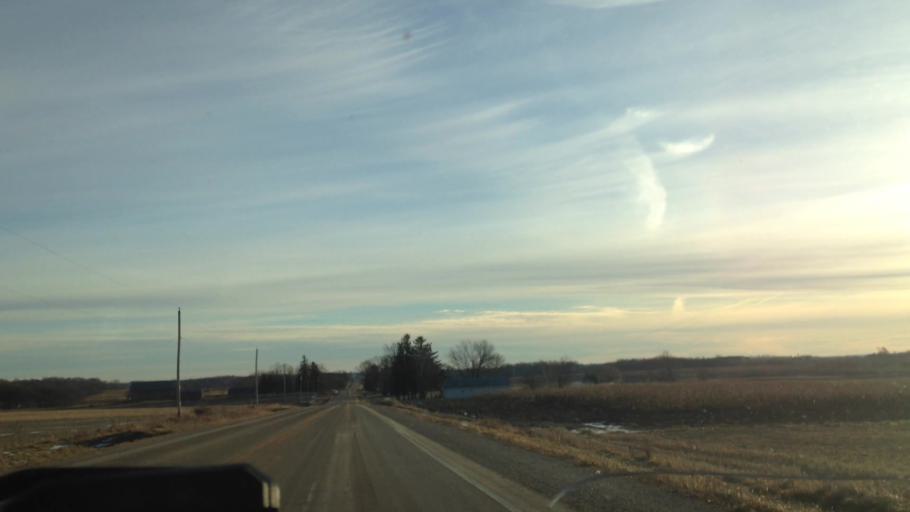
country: US
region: Wisconsin
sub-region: Dodge County
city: Theresa
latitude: 43.5366
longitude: -88.4891
